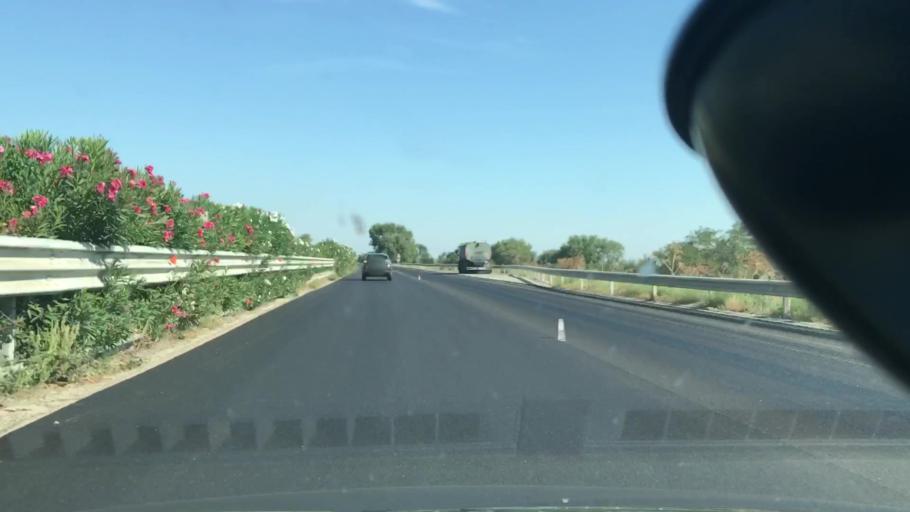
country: IT
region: Apulia
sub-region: Provincia di Foggia
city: Ascoli Satriano
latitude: 41.2714
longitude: 15.5526
